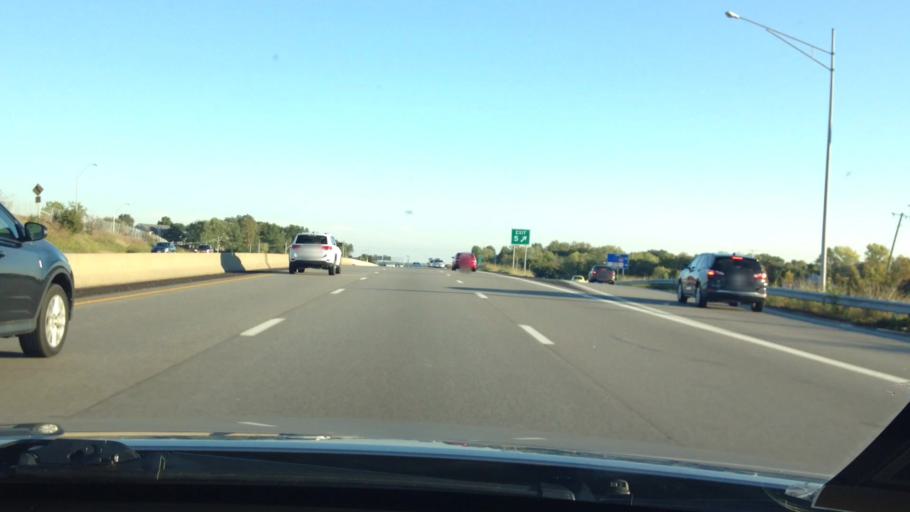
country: US
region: Missouri
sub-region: Platte County
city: Parkville
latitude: 39.2129
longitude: -94.6410
